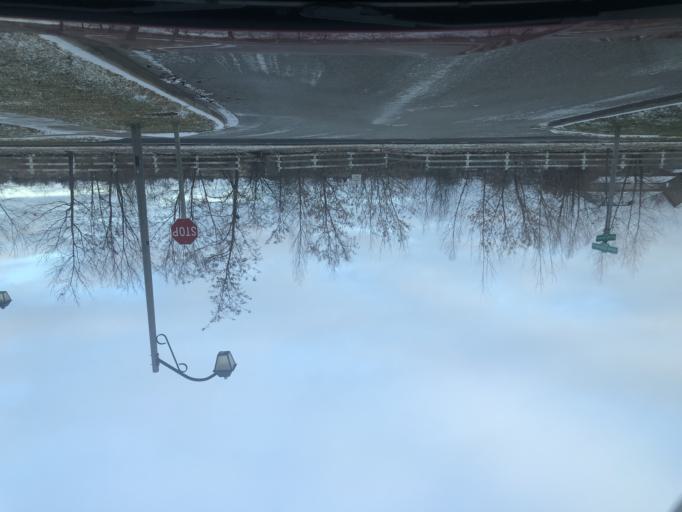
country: CA
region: Ontario
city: Markham
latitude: 43.8657
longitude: -79.2400
